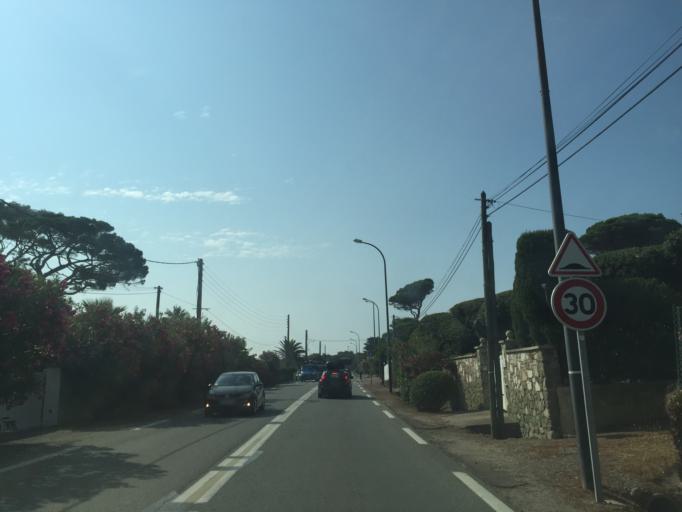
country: FR
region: Provence-Alpes-Cote d'Azur
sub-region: Departement du Var
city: Sainte-Maxime
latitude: 43.3162
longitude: 6.6674
